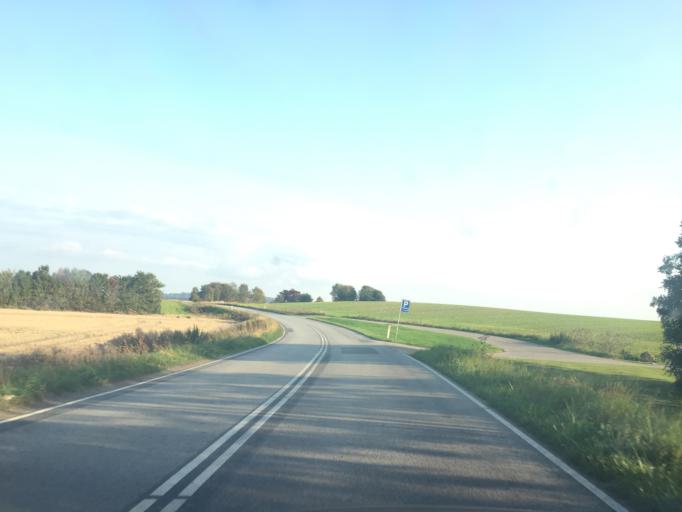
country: DK
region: Zealand
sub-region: Kalundborg Kommune
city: Svebolle
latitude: 55.6015
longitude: 11.2744
